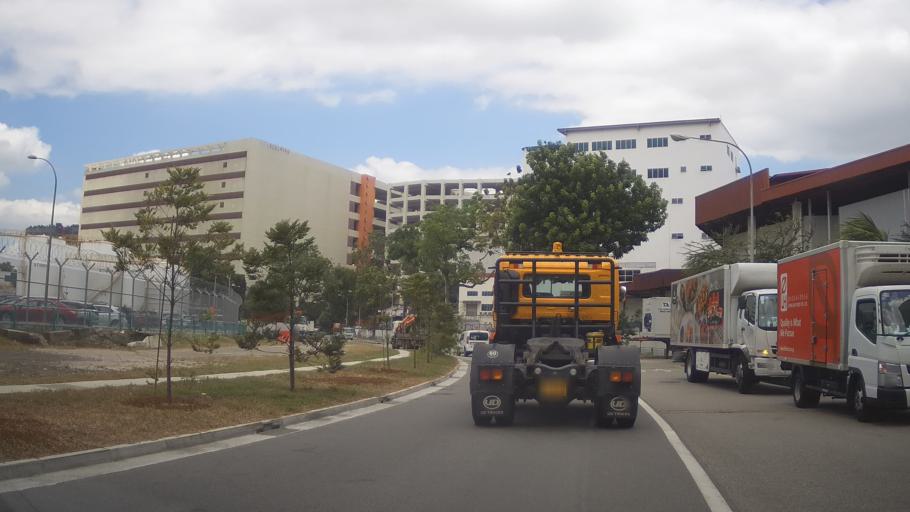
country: SG
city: Singapore
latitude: 1.3091
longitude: 103.7215
